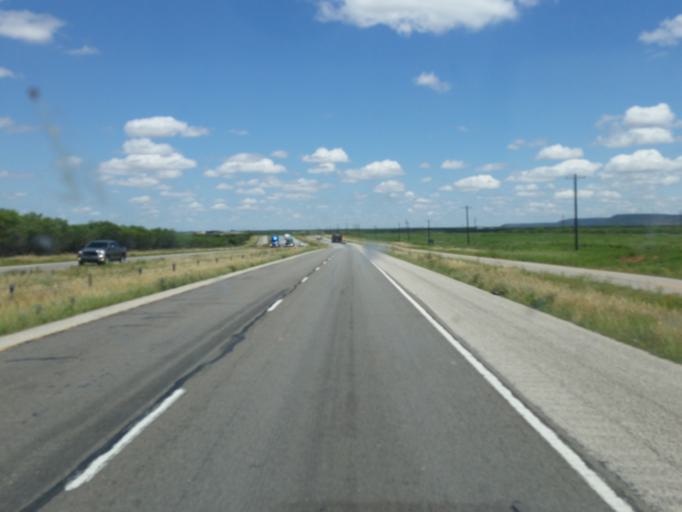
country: US
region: Texas
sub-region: Nolan County
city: Sweetwater
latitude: 32.4929
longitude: -100.2554
